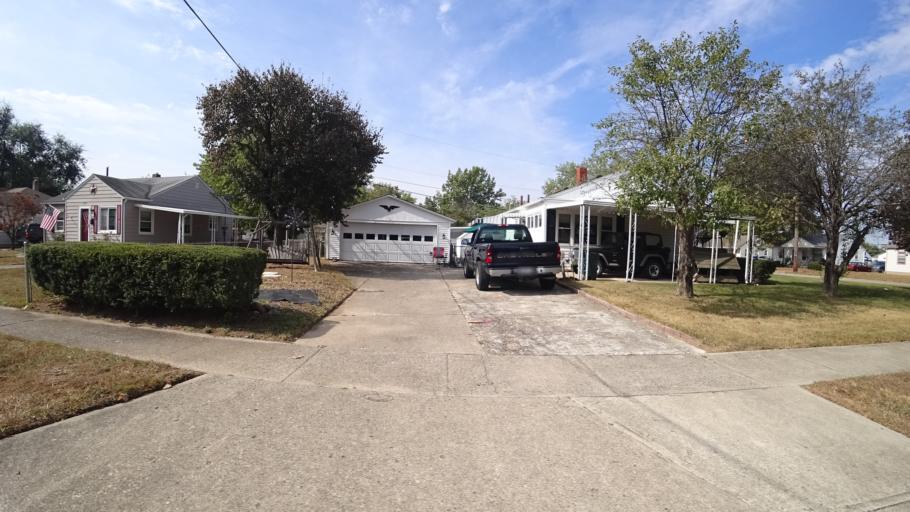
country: US
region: Ohio
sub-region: Butler County
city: Fairfield
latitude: 39.3604
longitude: -84.5484
